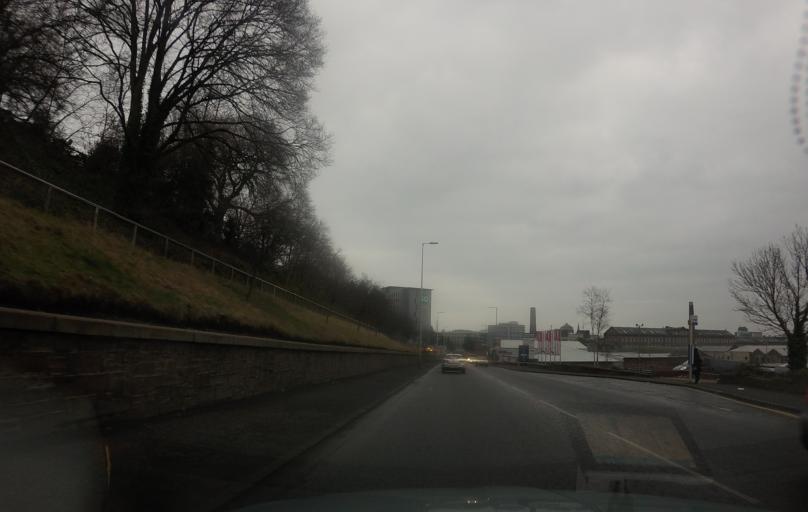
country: GB
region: Scotland
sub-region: Dundee City
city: Dundee
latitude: 56.4638
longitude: -2.9842
